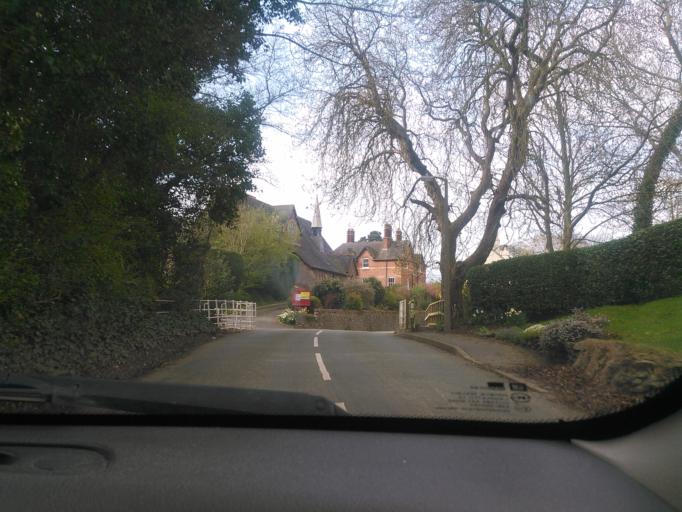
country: GB
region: England
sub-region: Shropshire
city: Great Hanwood
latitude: 52.6671
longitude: -2.8068
